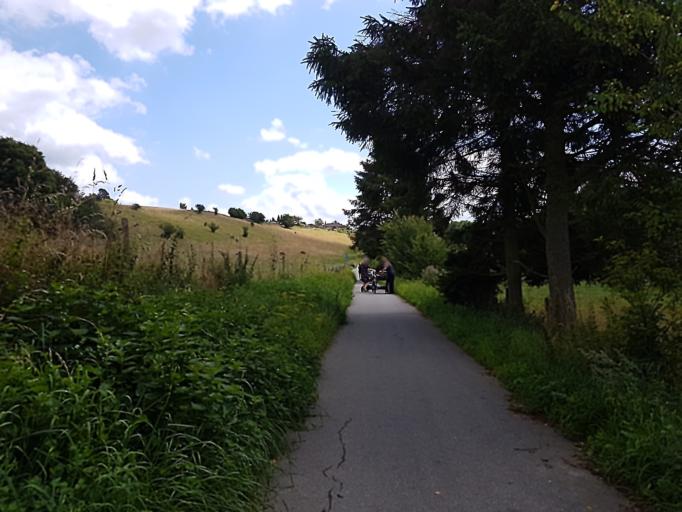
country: DK
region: Capital Region
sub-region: Egedal Kommune
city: Ganlose
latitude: 55.7936
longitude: 12.2540
